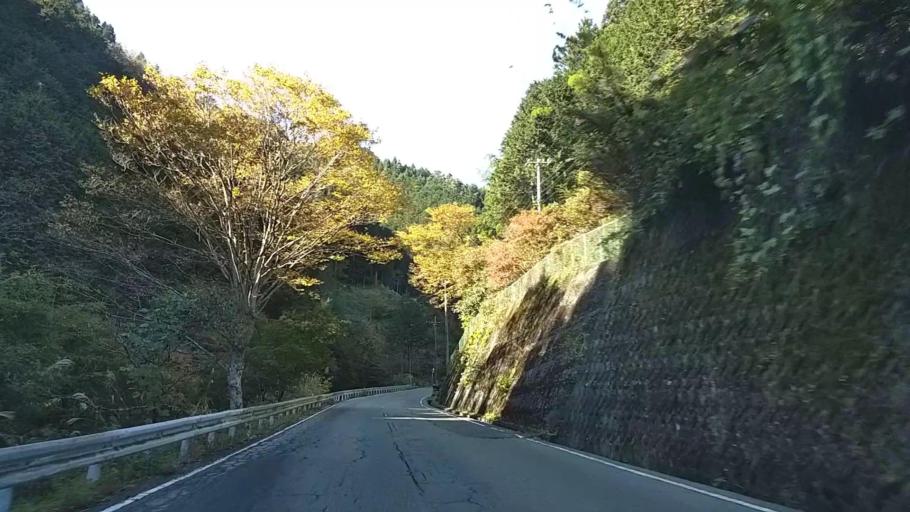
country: JP
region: Yamanashi
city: Uenohara
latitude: 35.6931
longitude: 139.0421
